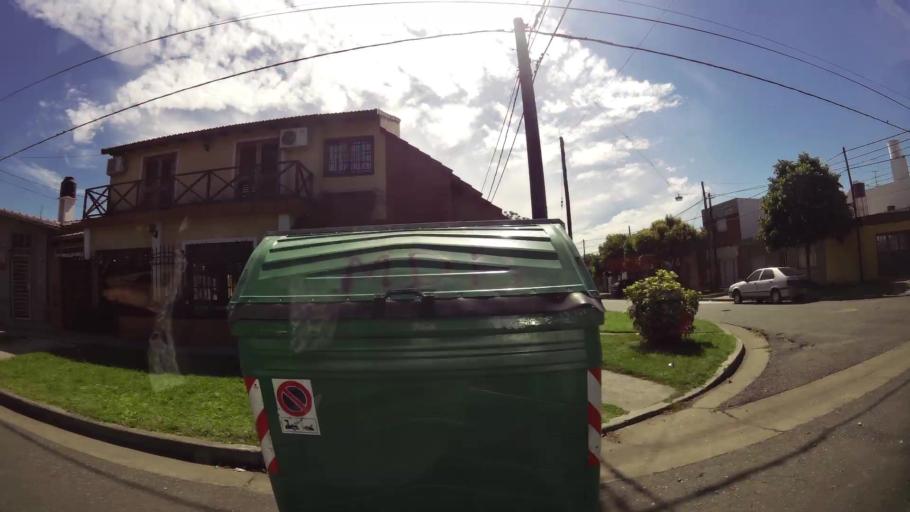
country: AR
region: Santa Fe
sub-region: Departamento de Rosario
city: Rosario
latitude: -32.9360
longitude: -60.7164
